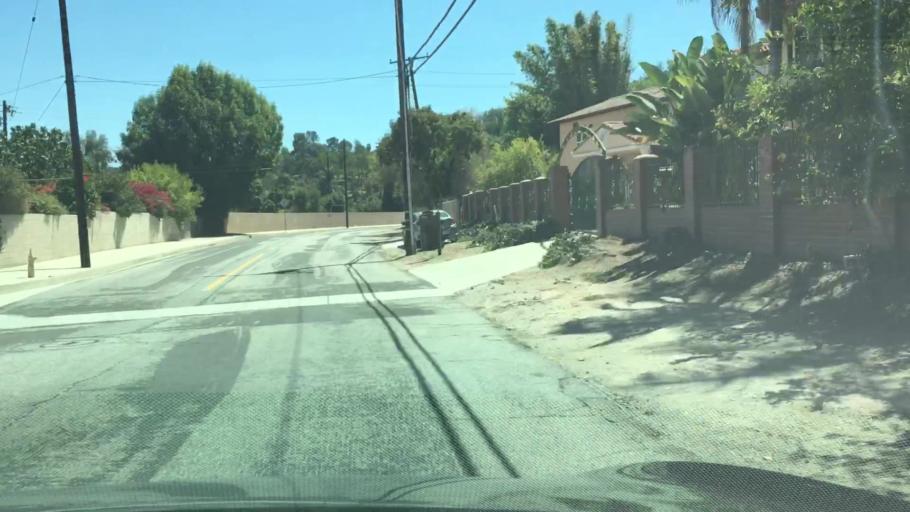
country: US
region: California
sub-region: Los Angeles County
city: Avocado Heights
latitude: 34.0089
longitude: -117.9924
